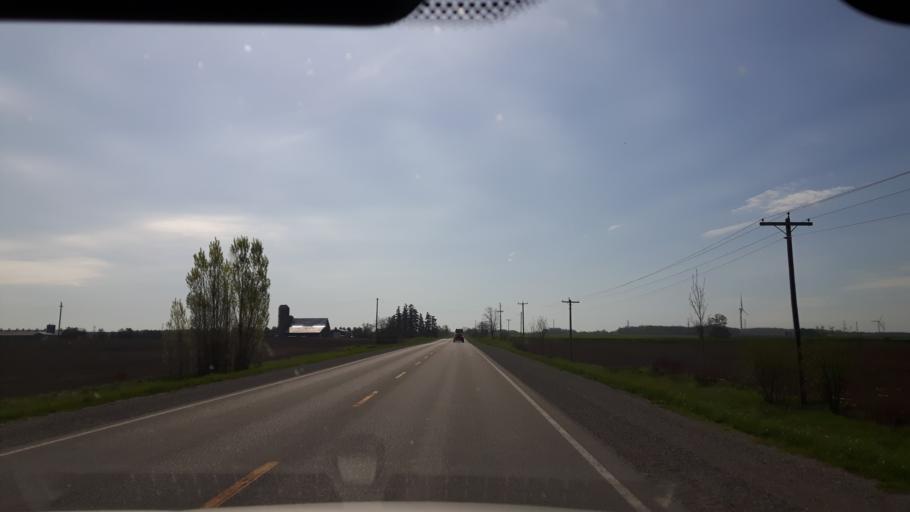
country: CA
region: Ontario
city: Bluewater
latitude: 43.5500
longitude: -81.6634
